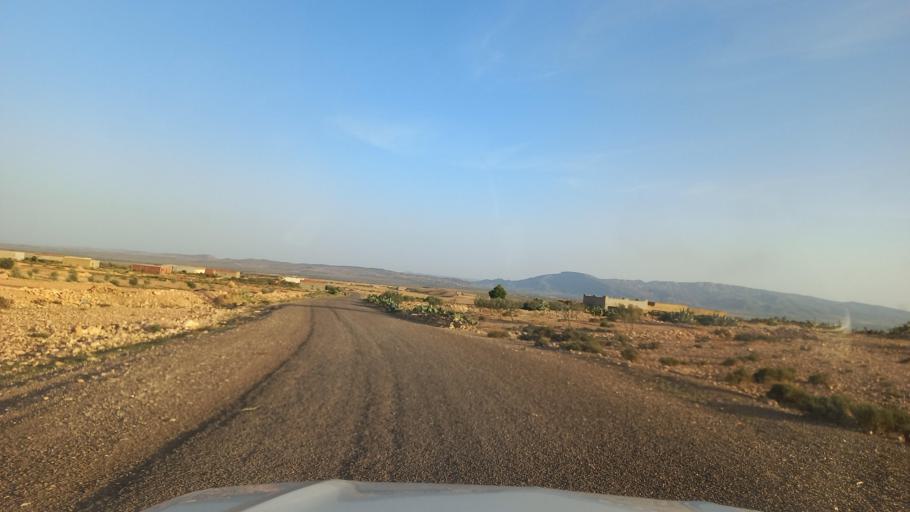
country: TN
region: Al Qasrayn
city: Kasserine
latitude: 35.2790
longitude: 8.9092
